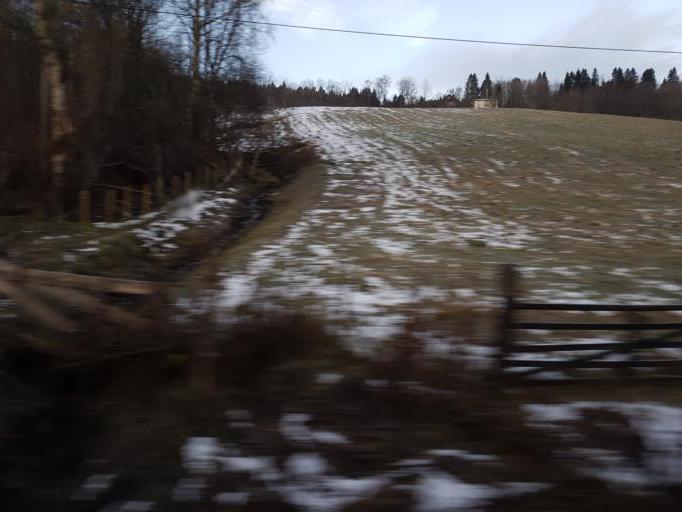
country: NO
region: Sor-Trondelag
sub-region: Midtre Gauldal
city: Storen
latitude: 62.9494
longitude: 10.1874
